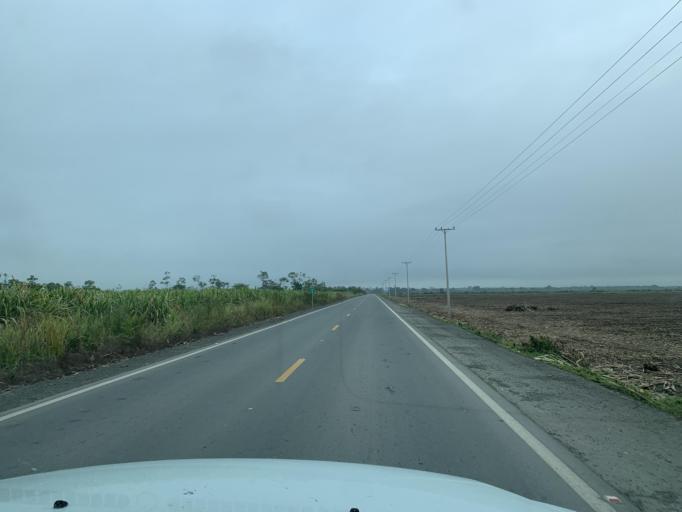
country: EC
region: Guayas
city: Coronel Marcelino Mariduena
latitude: -2.3061
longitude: -79.5042
